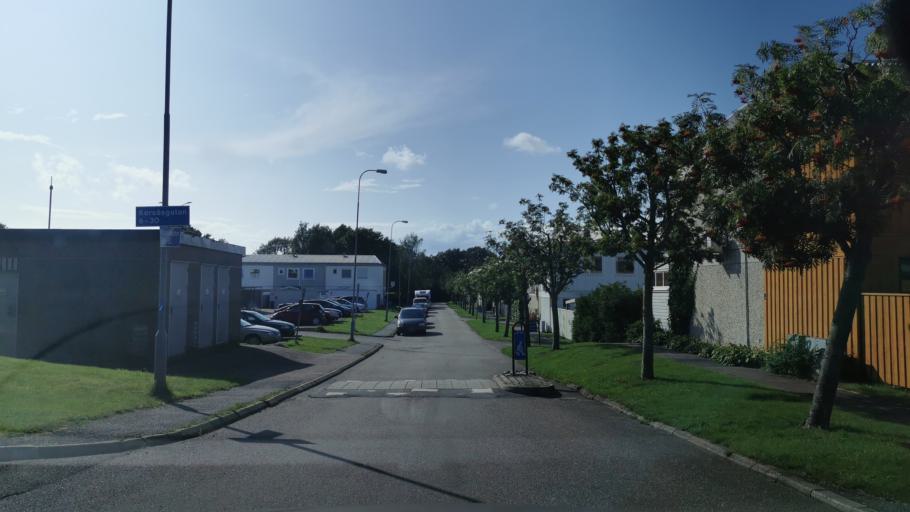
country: SE
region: Vaestra Goetaland
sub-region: Goteborg
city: Majorna
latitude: 57.6414
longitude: 11.9091
